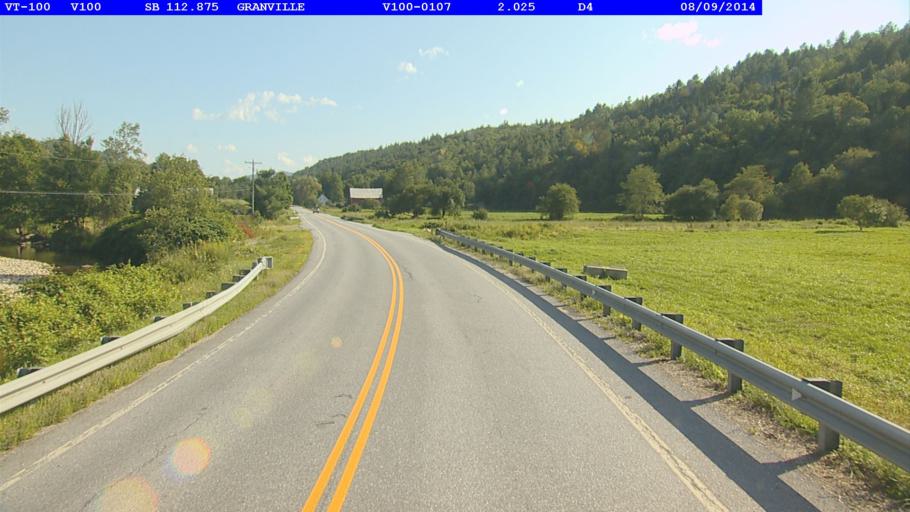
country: US
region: Vermont
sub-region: Orange County
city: Randolph
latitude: 43.9736
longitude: -72.8430
